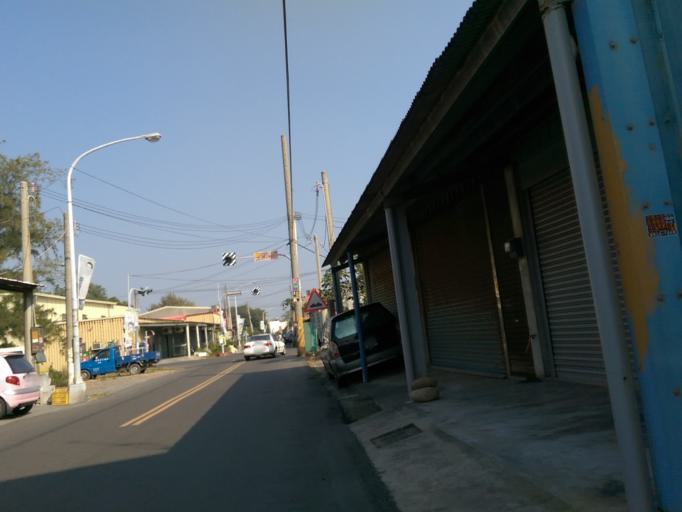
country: TW
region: Taiwan
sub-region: Yunlin
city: Douliu
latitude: 23.7514
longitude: 120.2530
